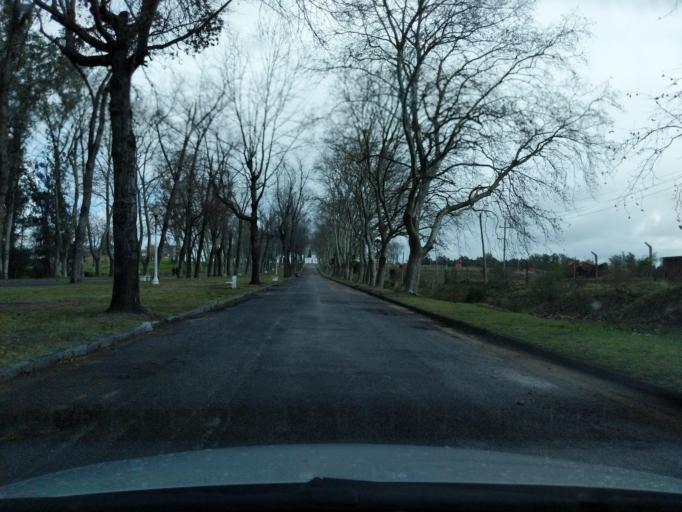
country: UY
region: Florida
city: Florida
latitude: -34.1055
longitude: -56.2252
